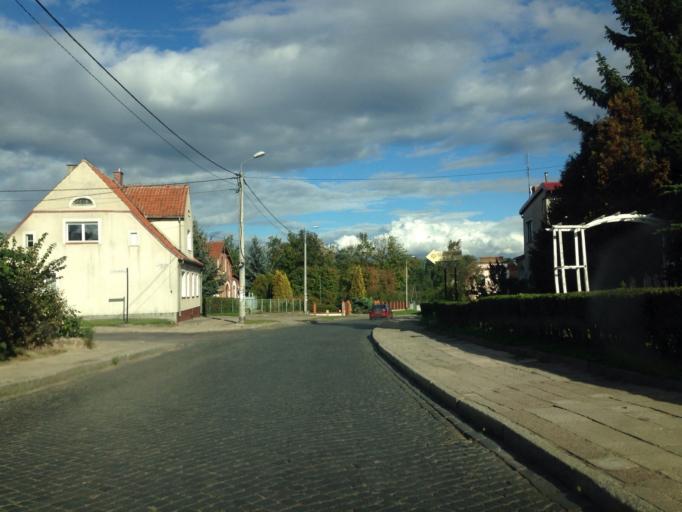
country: PL
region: Warmian-Masurian Voivodeship
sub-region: Powiat ilawski
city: Susz
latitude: 53.7194
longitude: 19.3380
